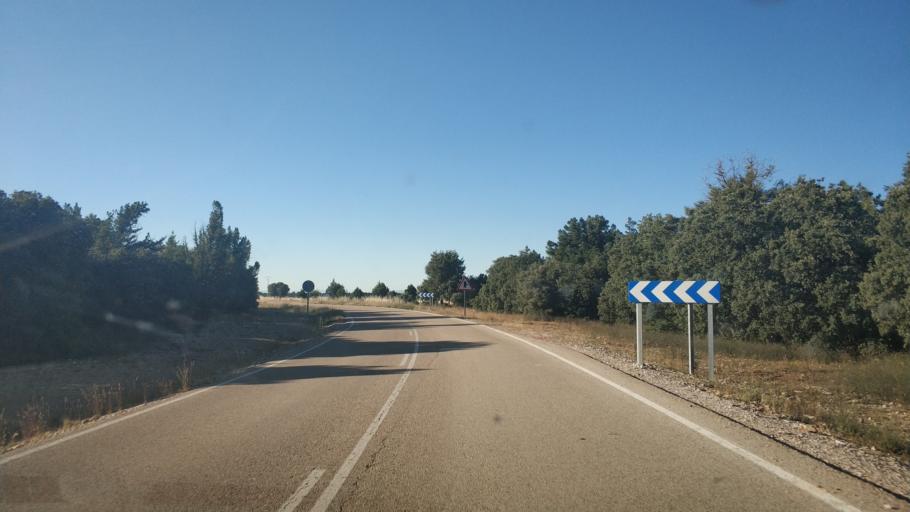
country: ES
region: Castille and Leon
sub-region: Provincia de Soria
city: Liceras
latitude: 41.4571
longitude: -3.2111
